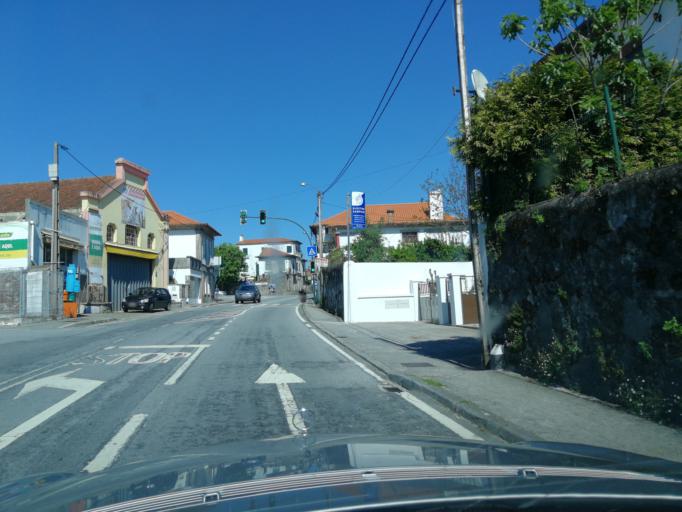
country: PT
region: Viana do Castelo
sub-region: Viana do Castelo
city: Meadela
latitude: 41.7088
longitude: -8.7765
